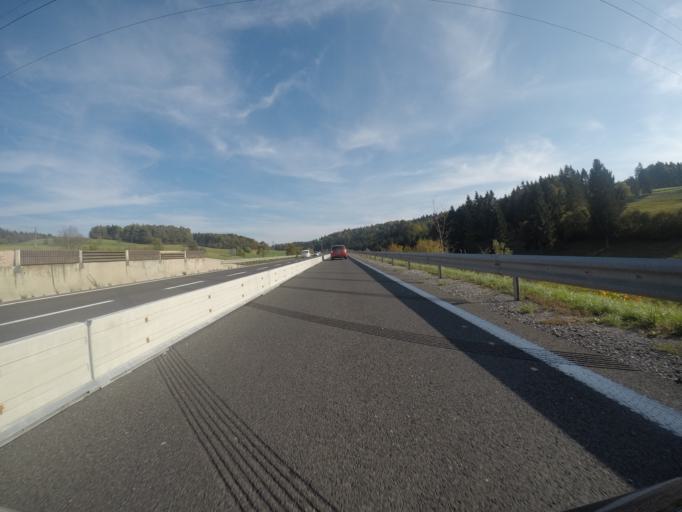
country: SI
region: Grosuplje
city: Grosuplje
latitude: 45.9764
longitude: 14.7055
